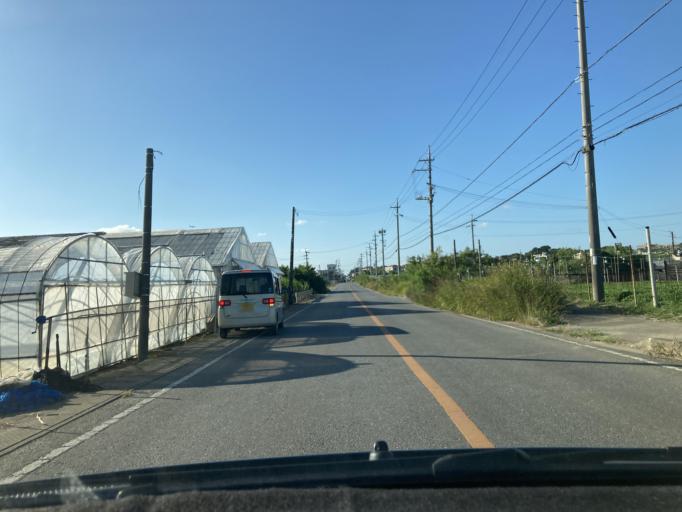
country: JP
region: Okinawa
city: Itoman
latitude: 26.1018
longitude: 127.6718
